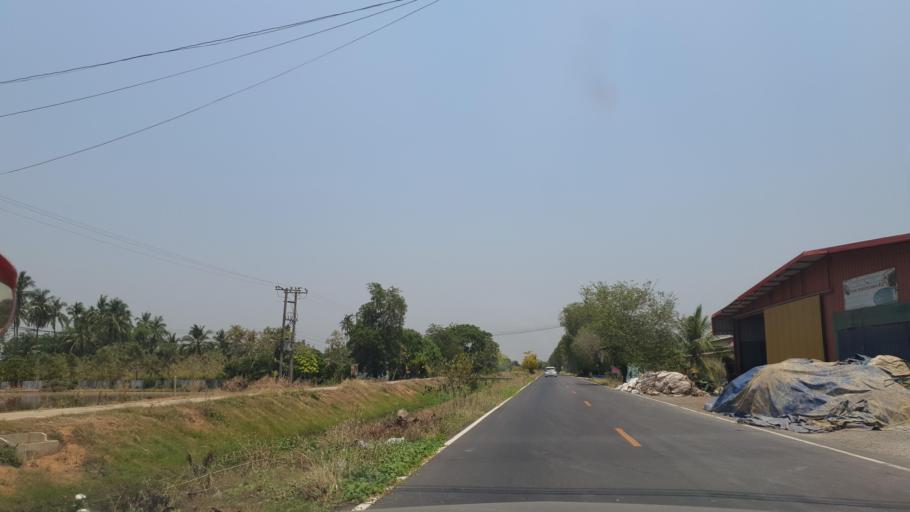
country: TH
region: Suphan Buri
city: Si Prachan
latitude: 14.6105
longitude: 100.1012
